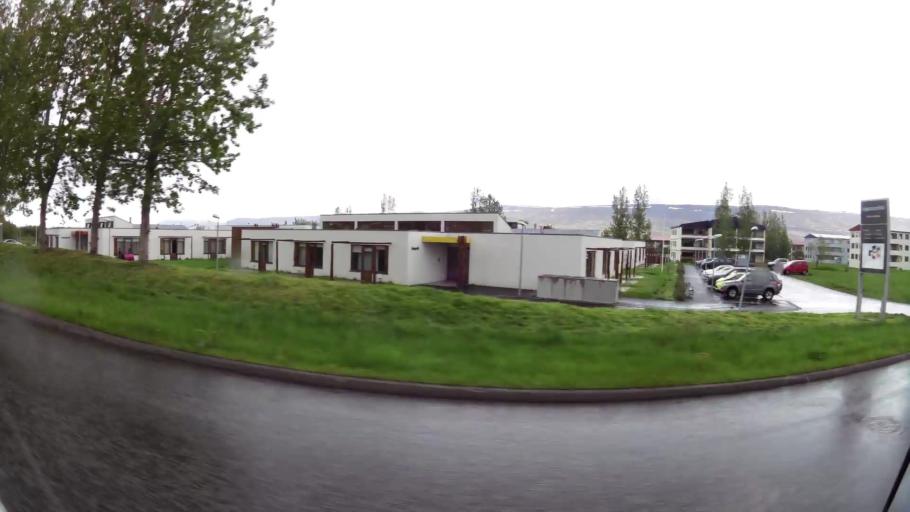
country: IS
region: Northeast
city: Akureyri
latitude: 65.6905
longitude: -18.1402
